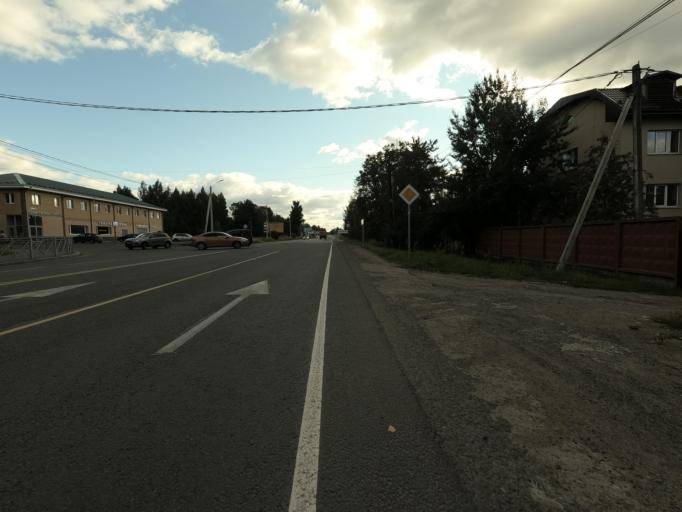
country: RU
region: Leningrad
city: Vsevolozhsk
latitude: 59.9893
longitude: 30.6572
